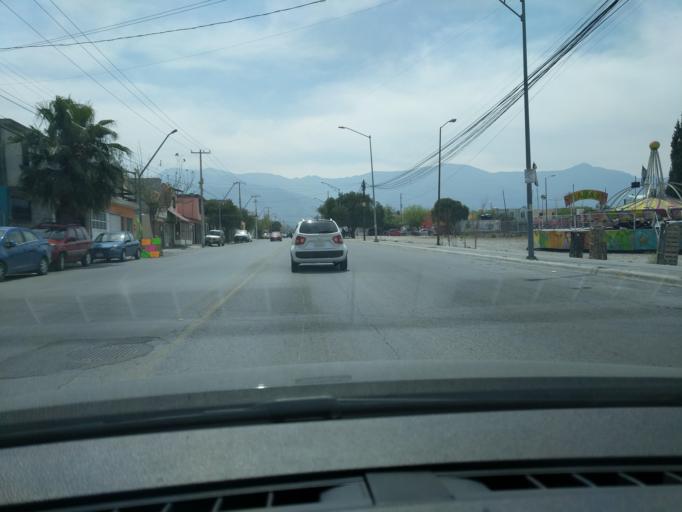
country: MX
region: Coahuila
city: Saltillo
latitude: 25.4228
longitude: -100.9448
